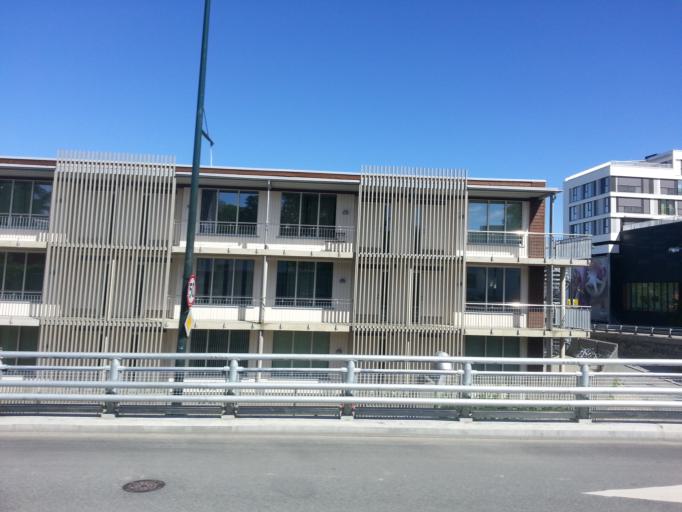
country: NO
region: Sor-Trondelag
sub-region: Trondheim
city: Trondheim
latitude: 63.4365
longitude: 10.4528
